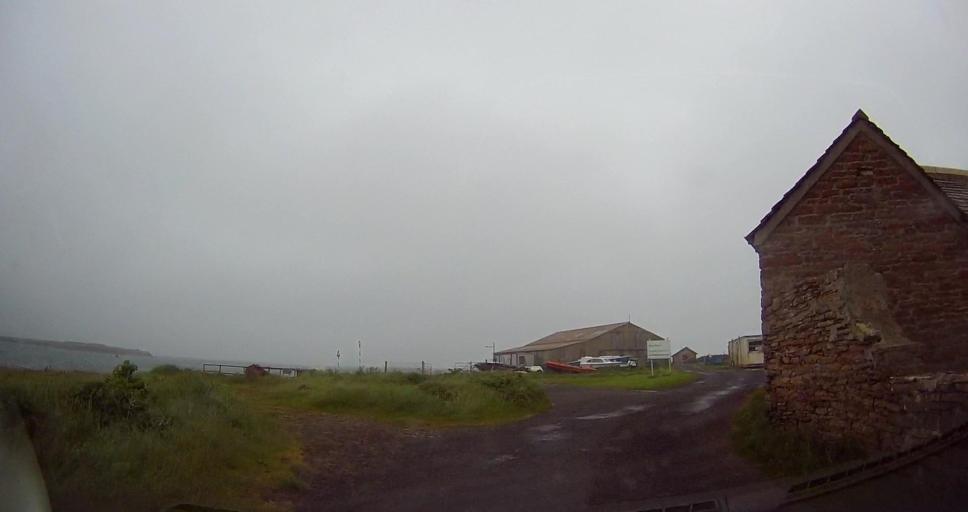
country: GB
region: Scotland
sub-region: Orkney Islands
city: Stromness
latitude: 58.9535
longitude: -3.2984
